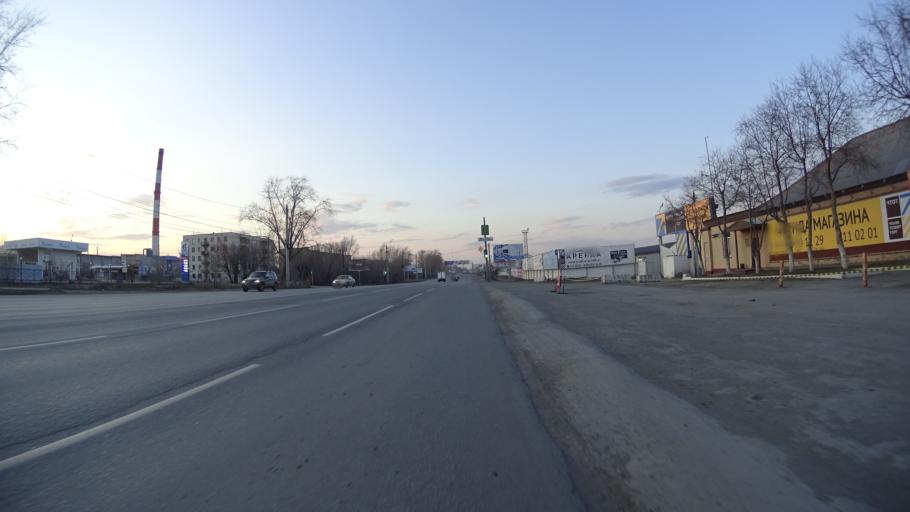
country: RU
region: Chelyabinsk
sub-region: Gorod Chelyabinsk
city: Chelyabinsk
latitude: 55.1062
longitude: 61.3873
